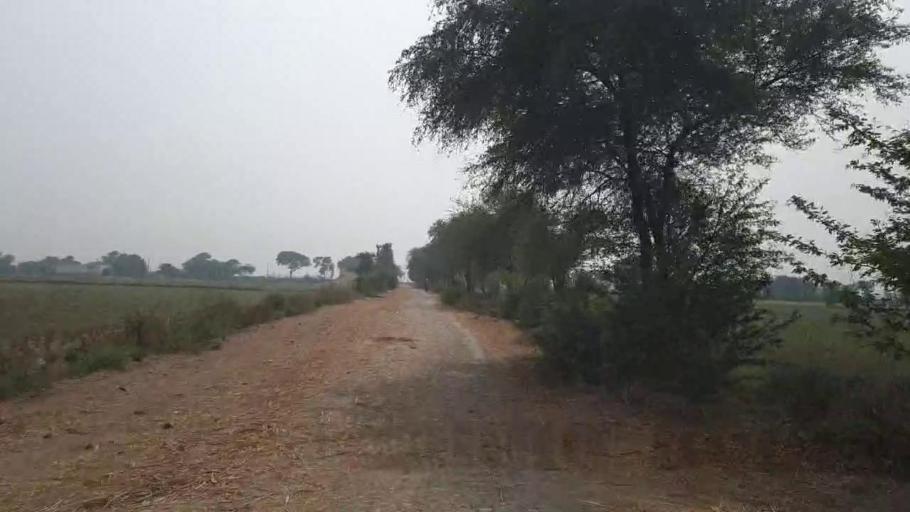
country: PK
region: Sindh
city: Kario
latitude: 24.6460
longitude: 68.6218
